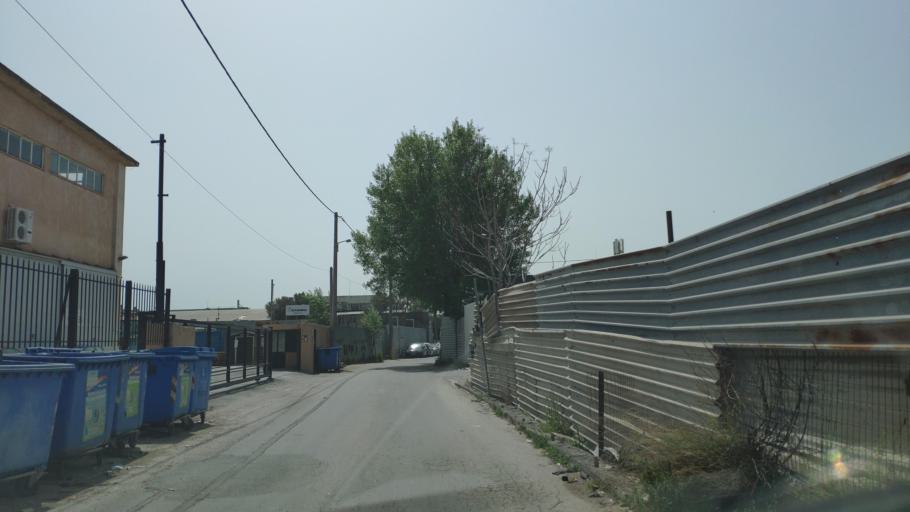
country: GR
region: Attica
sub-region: Nomarchia Athinas
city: Metamorfosi
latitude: 38.0766
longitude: 23.7695
